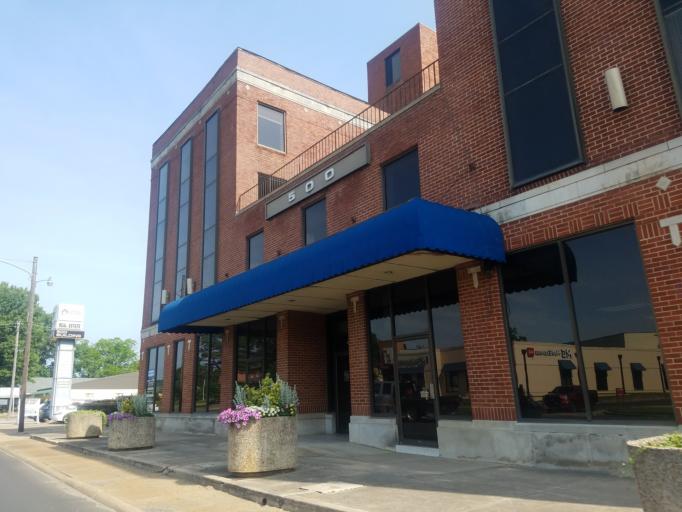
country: US
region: Arkansas
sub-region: Pope County
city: Russellville
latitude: 35.2791
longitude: -93.1370
